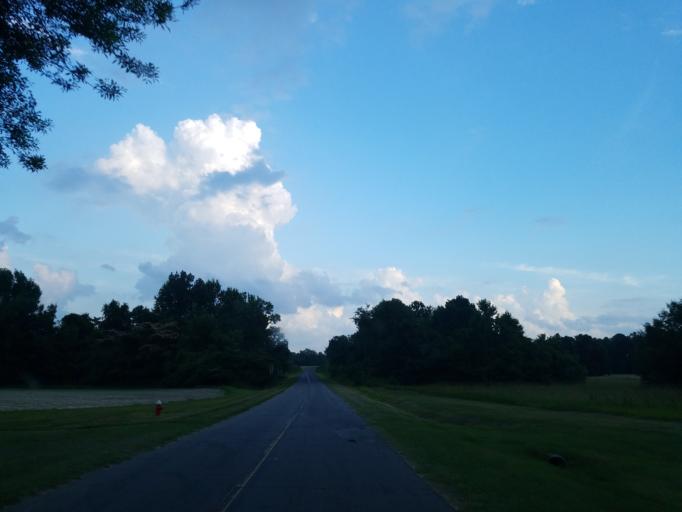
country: US
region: Georgia
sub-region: Dooly County
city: Unadilla
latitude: 32.1907
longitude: -83.7577
